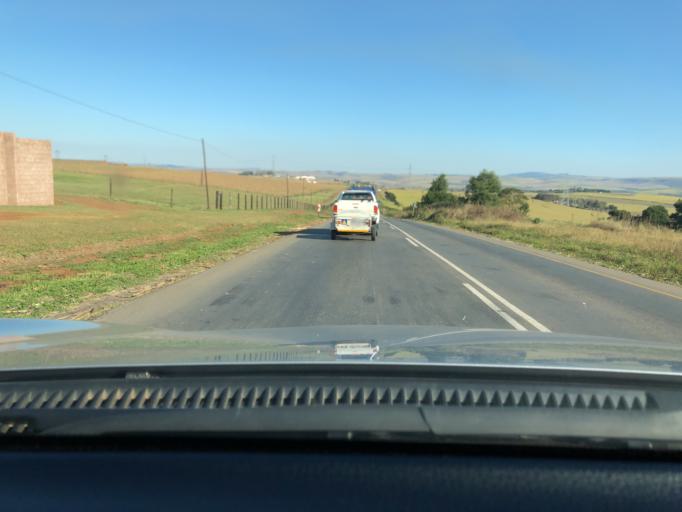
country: ZA
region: KwaZulu-Natal
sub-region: uMgungundlovu District Municipality
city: Camperdown
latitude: -29.7589
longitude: 30.5070
